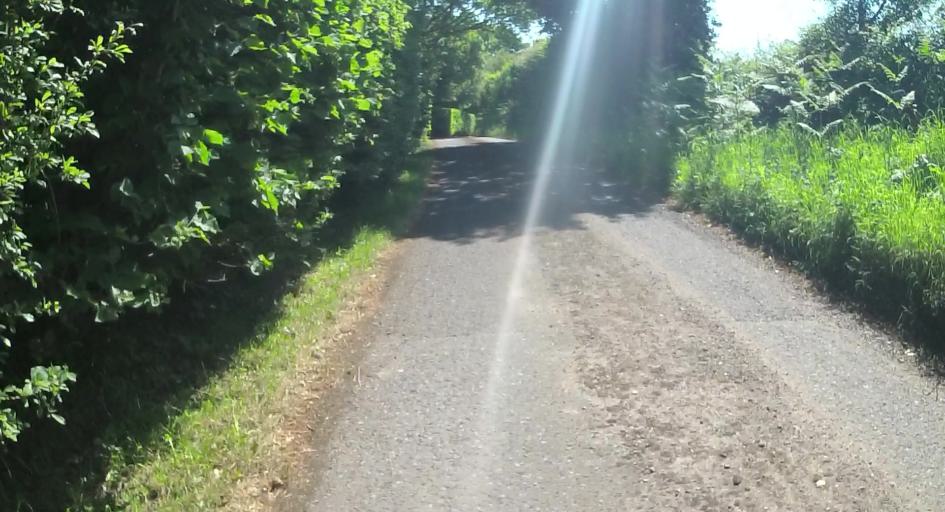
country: GB
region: England
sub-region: Hampshire
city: Kingsclere
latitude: 51.3483
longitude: -1.2748
